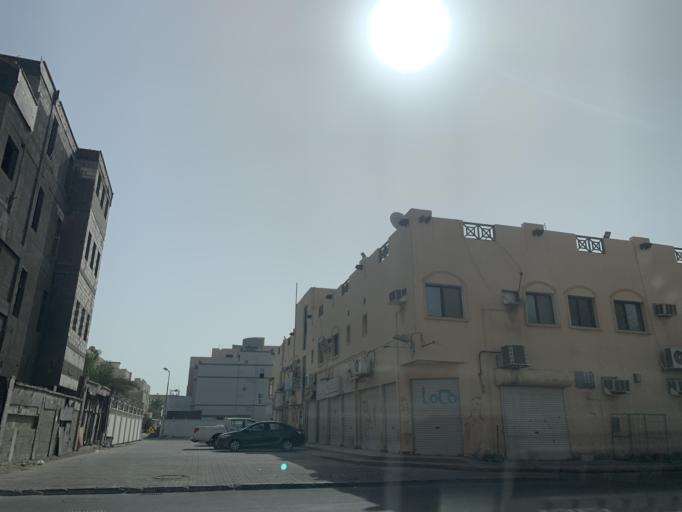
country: BH
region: Northern
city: Ar Rifa'
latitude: 26.1456
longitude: 50.5821
